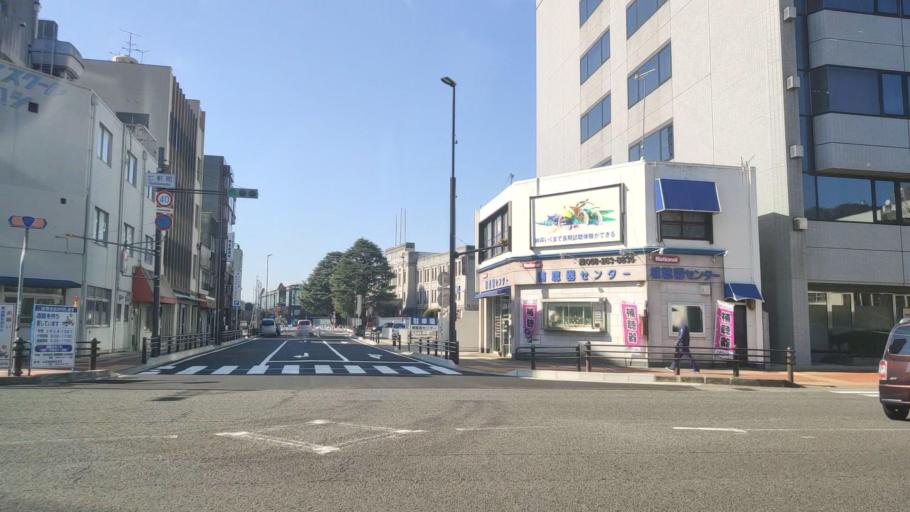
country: JP
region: Gifu
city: Gifu-shi
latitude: 35.4265
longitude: 136.7627
